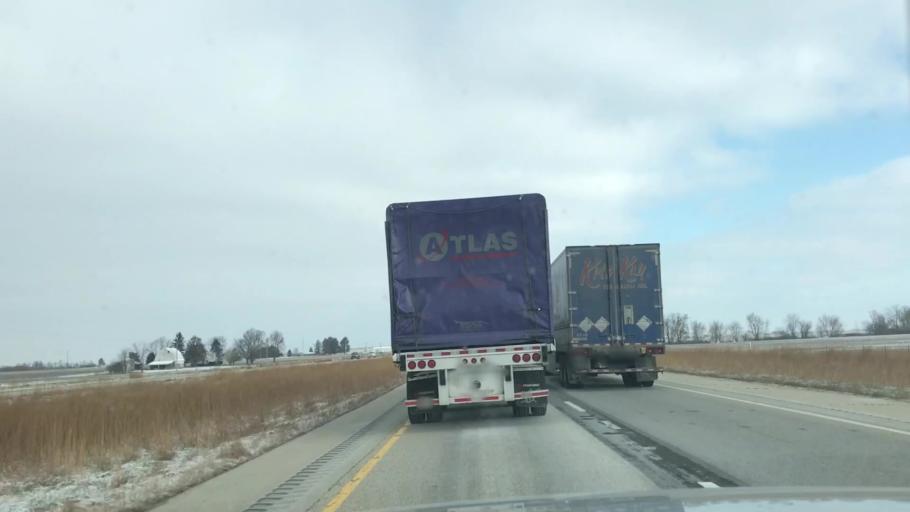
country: US
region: Illinois
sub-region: Sangamon County
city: Divernon
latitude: 39.5155
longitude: -89.6454
